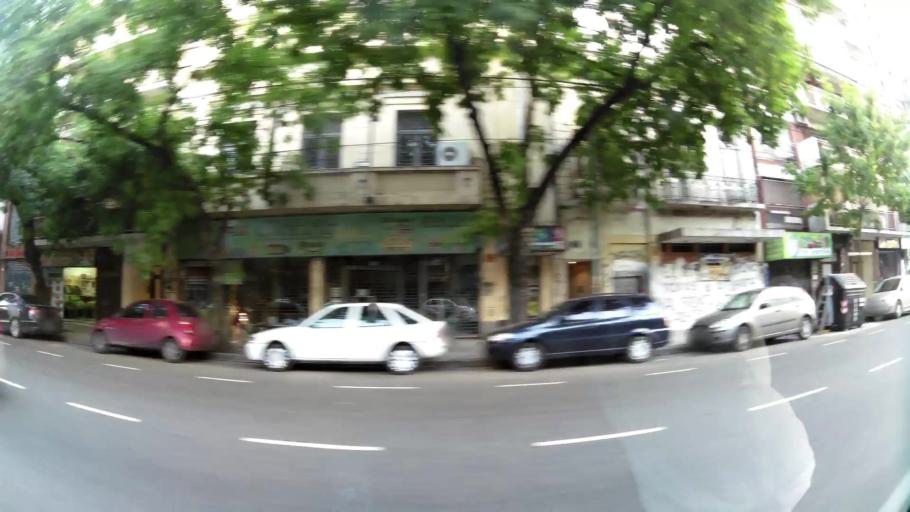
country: AR
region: Buenos Aires F.D.
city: Colegiales
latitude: -34.6010
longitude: -58.4407
